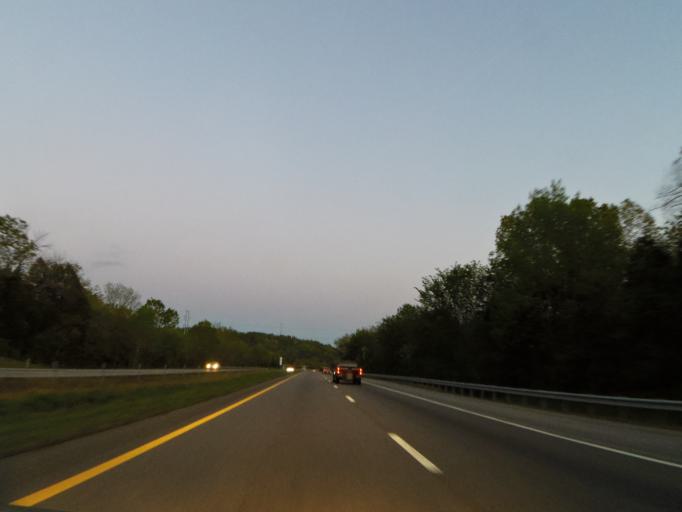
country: US
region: Tennessee
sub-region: Anderson County
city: Norris
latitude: 36.1619
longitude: -84.0765
